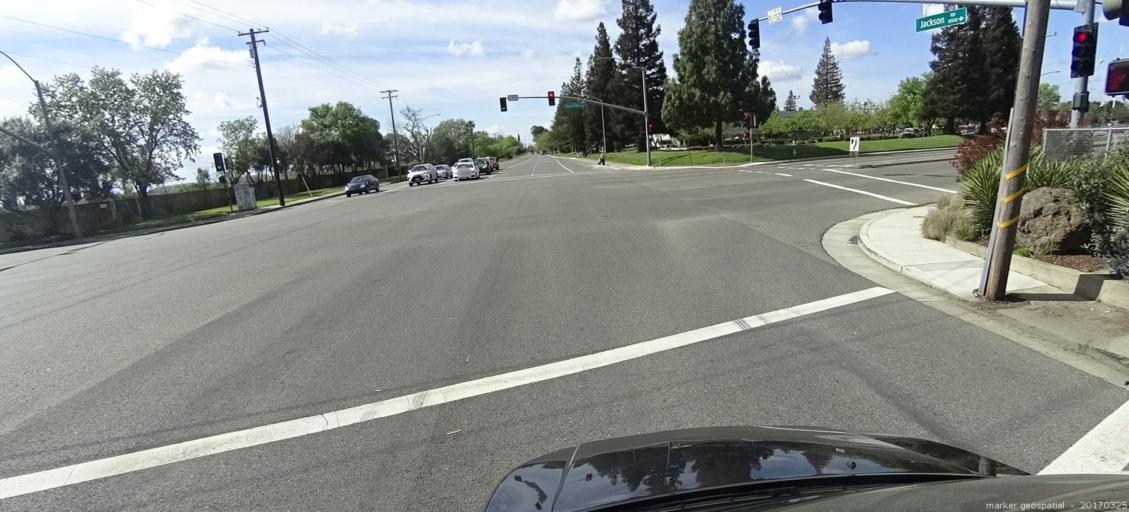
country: US
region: California
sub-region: Sacramento County
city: Rosemont
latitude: 38.5444
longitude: -121.3907
